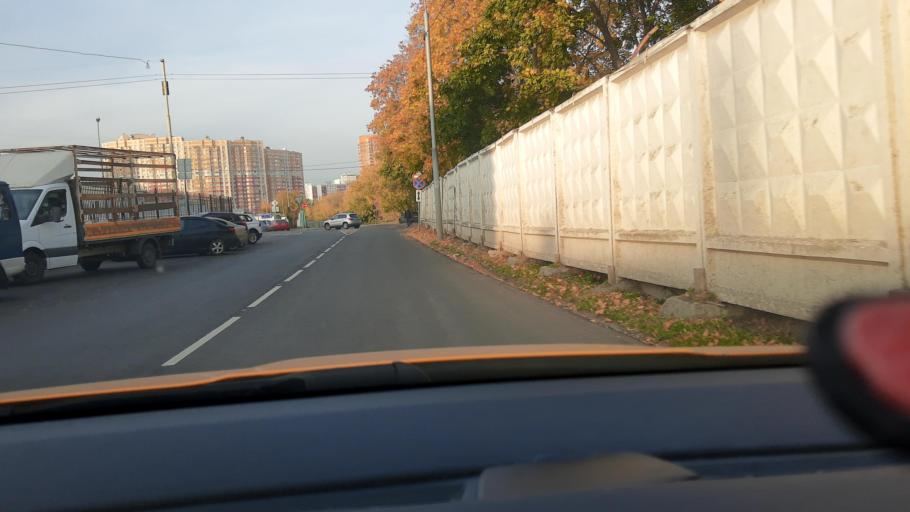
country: RU
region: Moscow
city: Strogino
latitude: 55.7883
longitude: 37.3987
